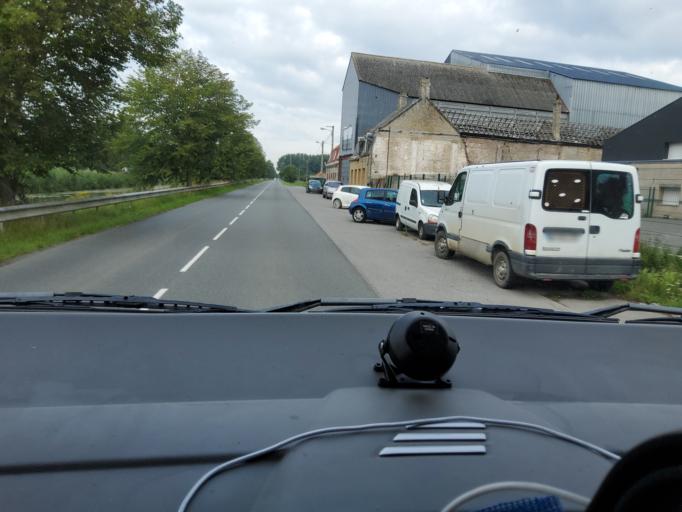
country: FR
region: Nord-Pas-de-Calais
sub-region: Departement du Nord
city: Bierne
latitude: 50.9709
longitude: 2.4160
